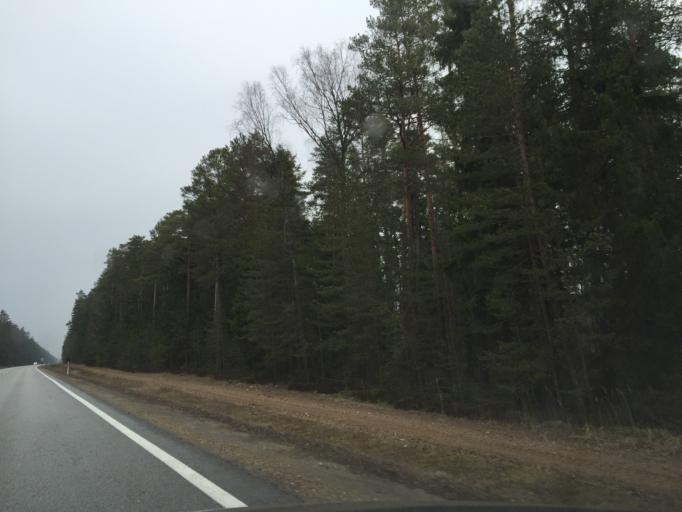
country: LV
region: Salacgrivas
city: Salacgriva
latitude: 57.5289
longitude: 24.4309
